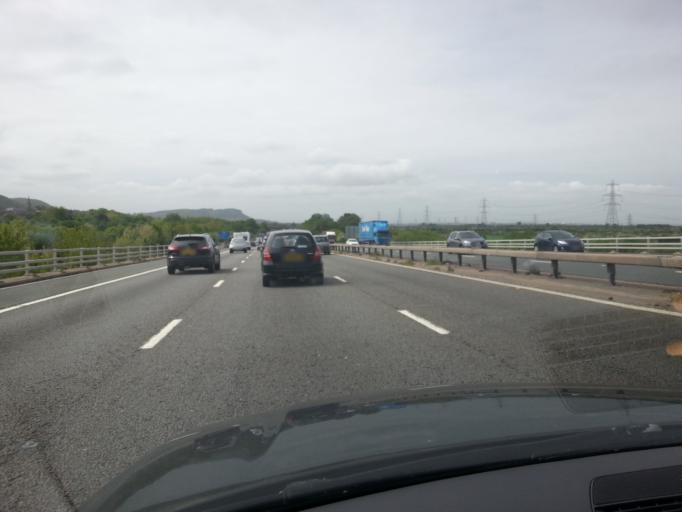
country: GB
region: England
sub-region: Cheshire West and Chester
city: Frodsham
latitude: 53.3062
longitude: -2.7147
